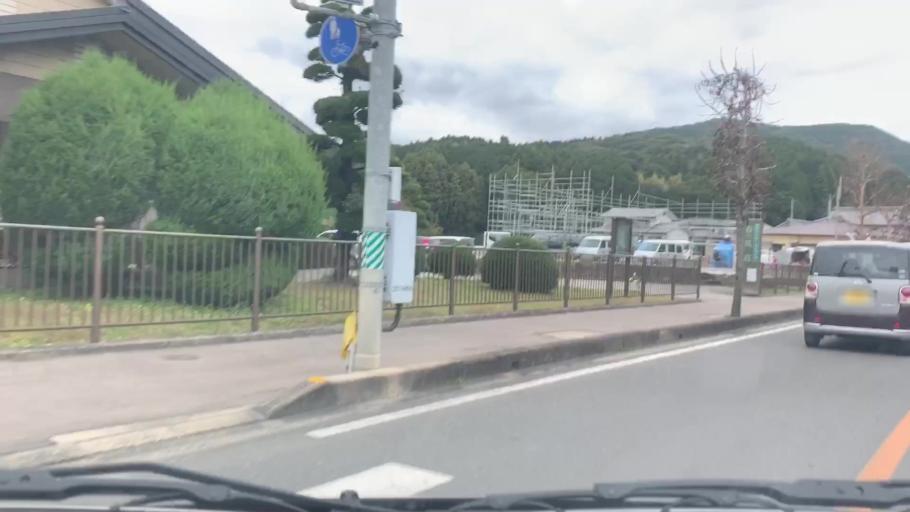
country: JP
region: Saga Prefecture
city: Ureshinomachi-shimojuku
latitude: 33.1014
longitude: 129.9991
